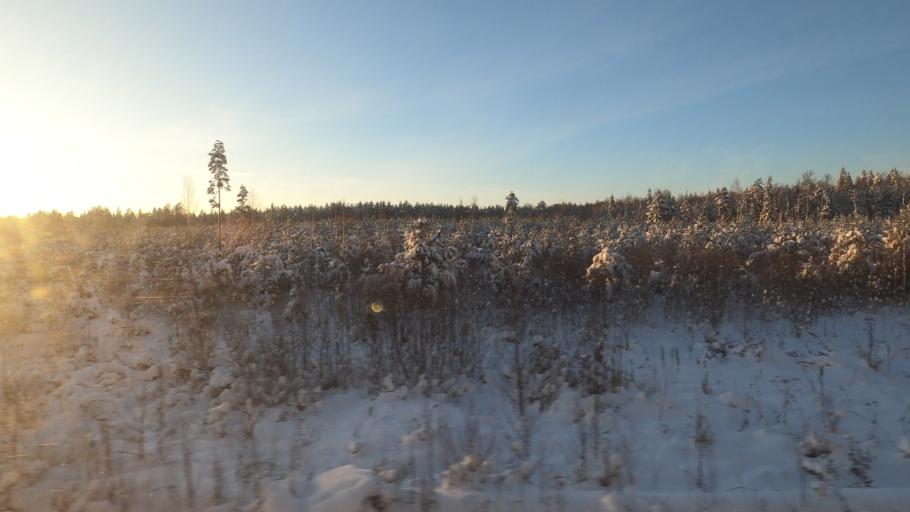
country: RU
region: Moskovskaya
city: Verbilki
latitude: 56.5202
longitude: 37.5572
